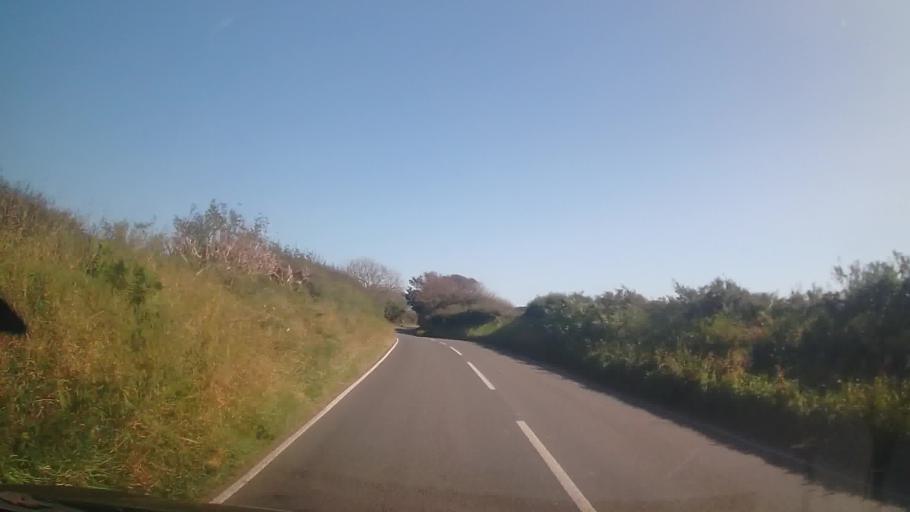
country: GB
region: Wales
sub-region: Pembrokeshire
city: Mathry
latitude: 51.9434
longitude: -5.0695
